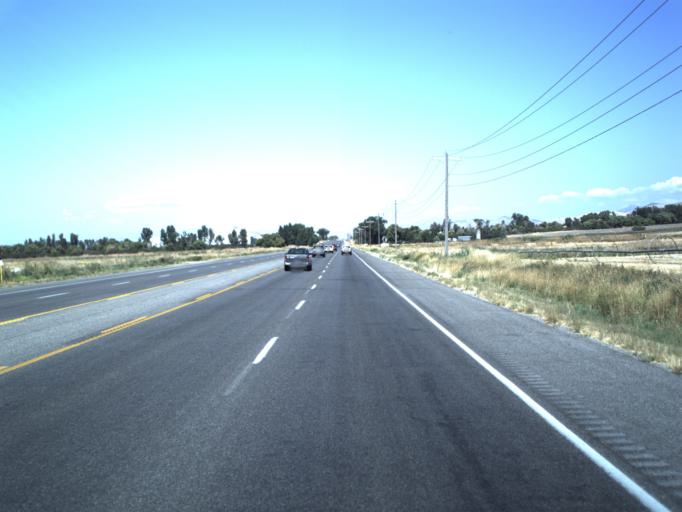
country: US
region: Utah
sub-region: Cache County
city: Richmond
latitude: 41.9299
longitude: -111.8141
